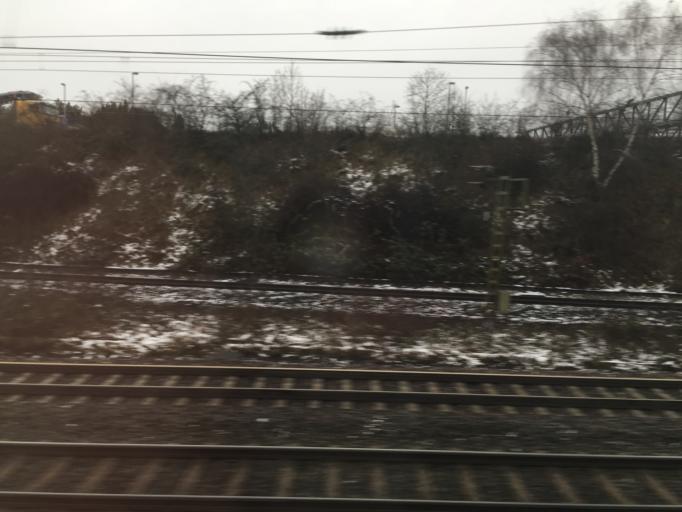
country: DE
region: Baden-Wuerttemberg
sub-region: Regierungsbezirk Stuttgart
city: Ludwigsburg
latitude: 48.8841
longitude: 9.1888
